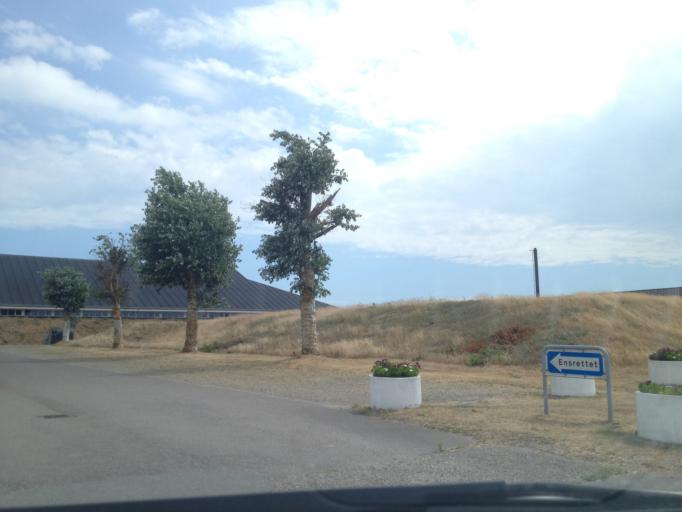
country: DK
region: Central Jutland
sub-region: Syddjurs Kommune
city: Ebeltoft
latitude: 56.1524
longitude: 10.6935
